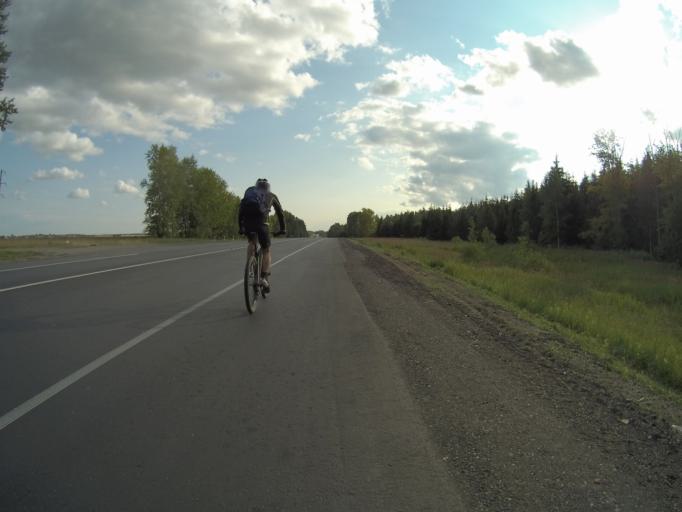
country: RU
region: Vladimir
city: Suzdal'
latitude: 56.4702
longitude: 40.4800
